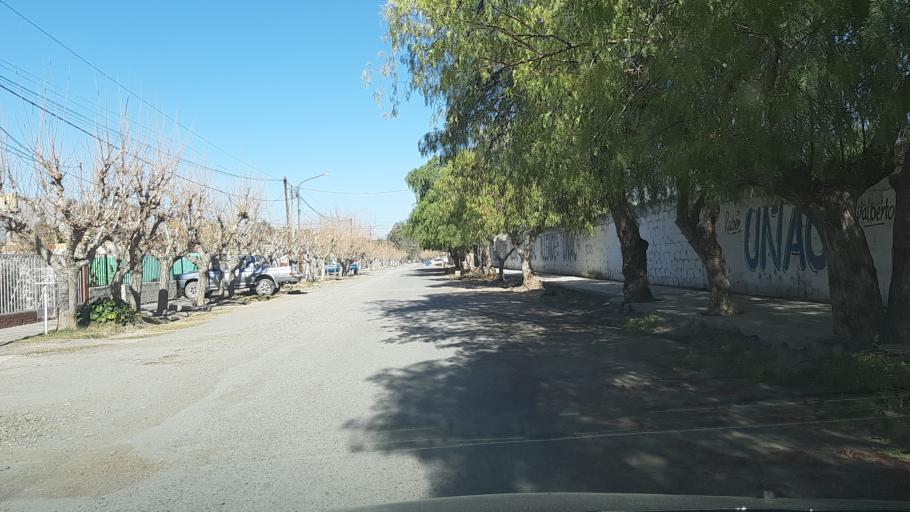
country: AR
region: San Juan
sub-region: Departamento de Zonda
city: Zonda
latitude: -31.5471
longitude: -68.7273
